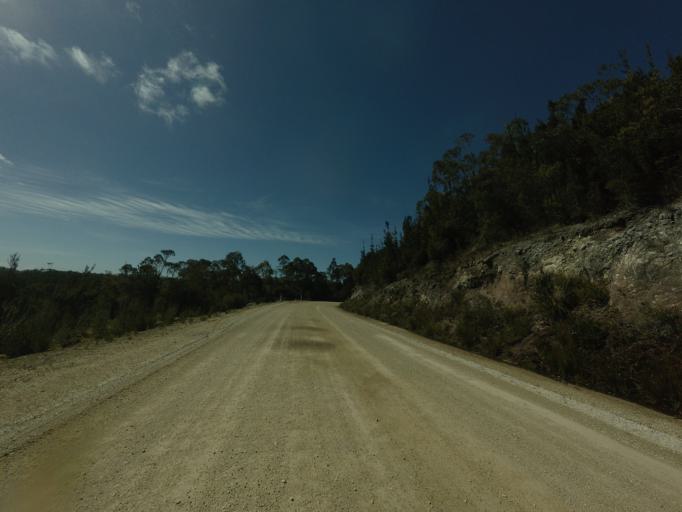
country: AU
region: Tasmania
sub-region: Huon Valley
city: Geeveston
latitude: -42.8202
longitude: 146.3892
